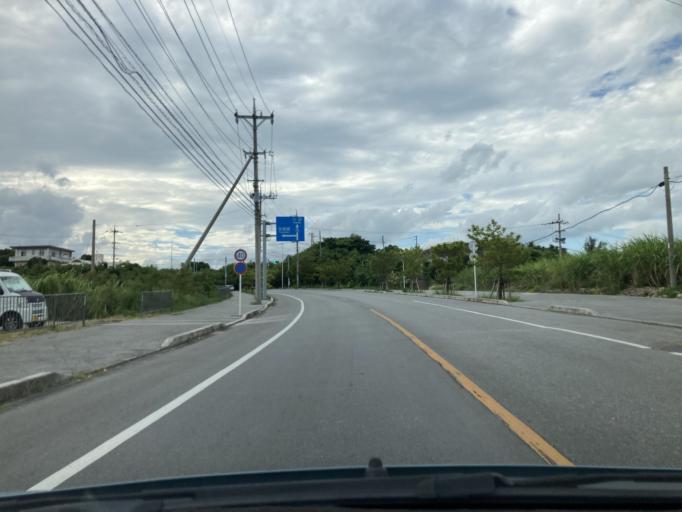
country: JP
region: Okinawa
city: Katsuren-haebaru
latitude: 26.3280
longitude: 127.8957
